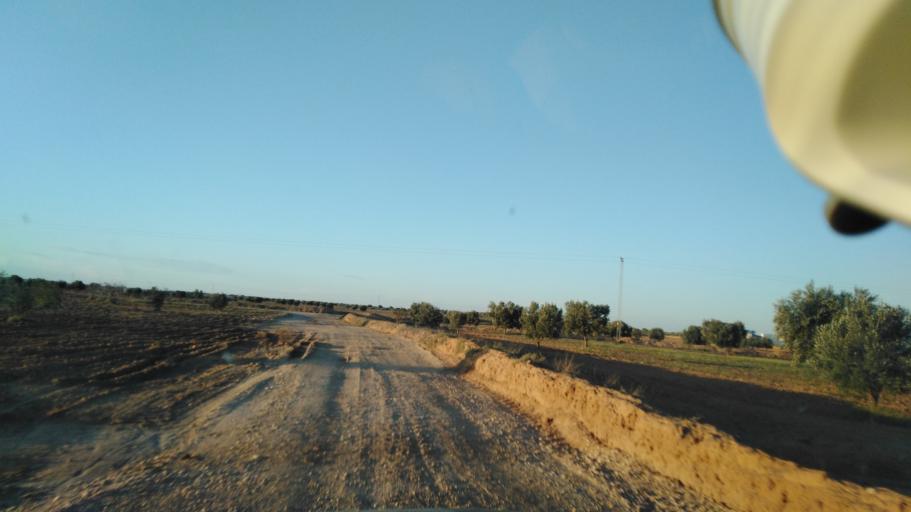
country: TN
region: Safaqis
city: Bi'r `Ali Bin Khalifah
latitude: 34.6733
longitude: 10.3833
